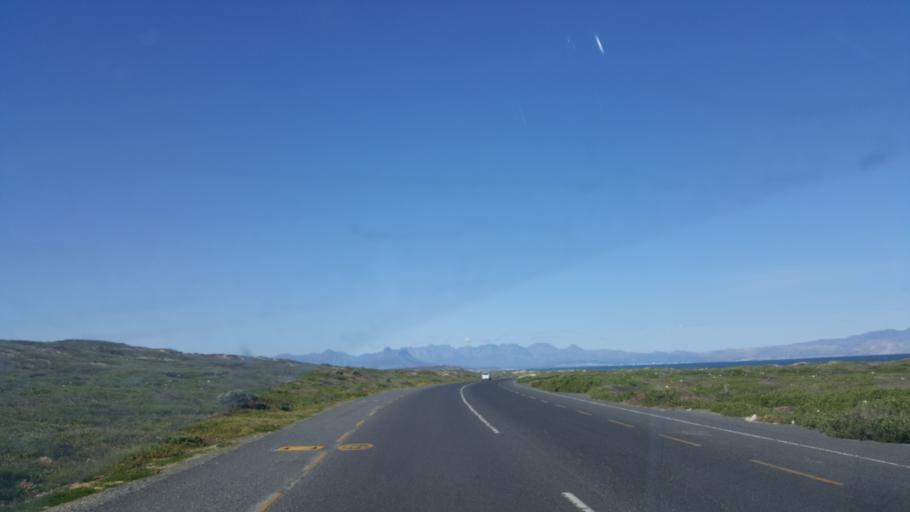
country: ZA
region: Western Cape
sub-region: City of Cape Town
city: Retreat
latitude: -34.0771
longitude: 18.5916
